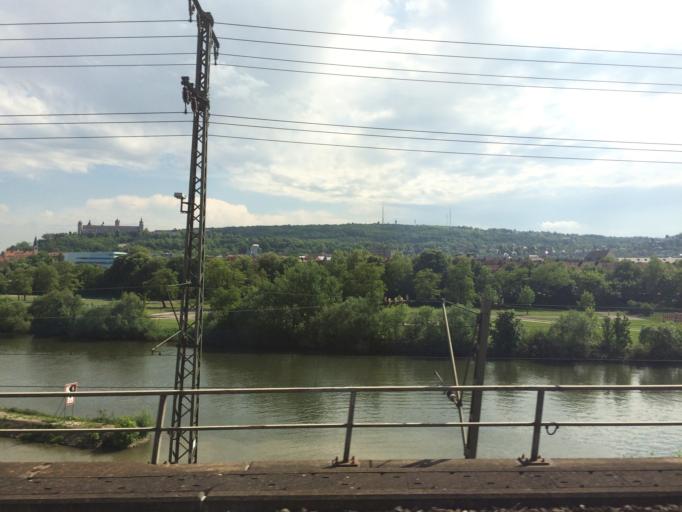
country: DE
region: Bavaria
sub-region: Regierungsbezirk Unterfranken
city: Wuerzburg
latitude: 49.8042
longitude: 9.9173
